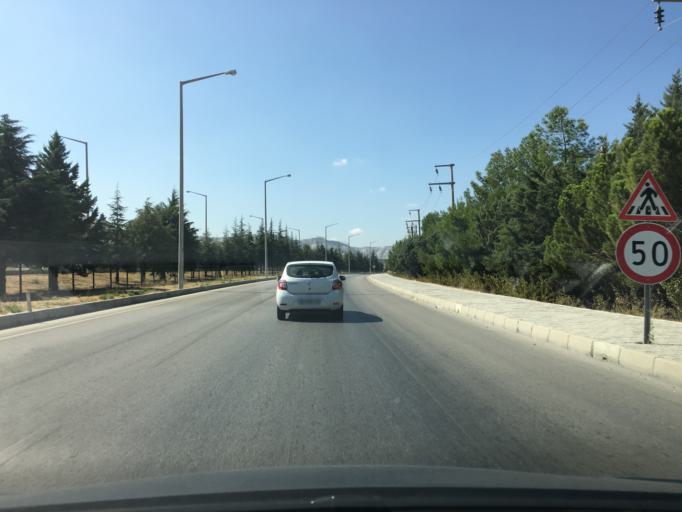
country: TR
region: Burdur
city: Burdur
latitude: 37.7344
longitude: 30.3098
